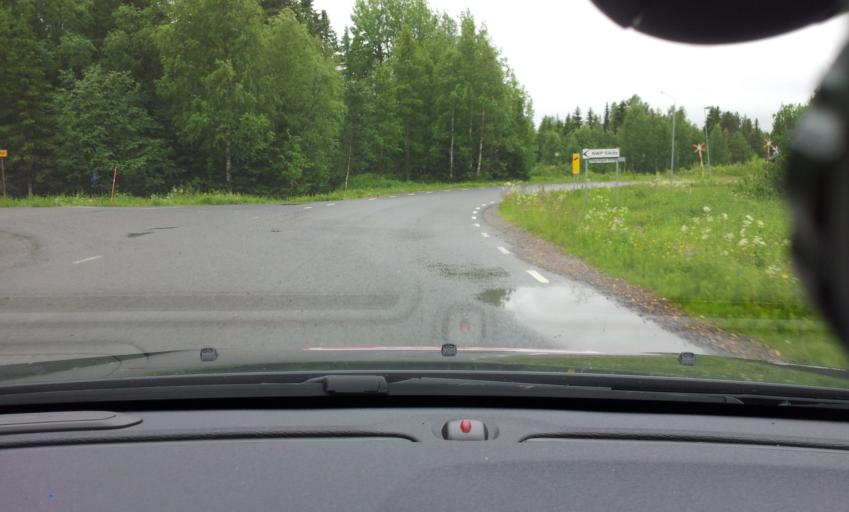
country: SE
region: Jaemtland
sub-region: Stroemsunds Kommun
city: Stroemsund
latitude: 63.6245
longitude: 15.2016
